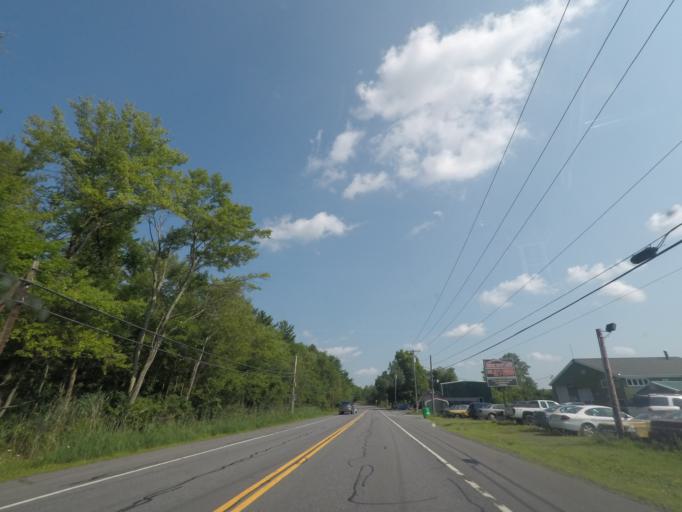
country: US
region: New York
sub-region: Rensselaer County
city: Nassau
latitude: 42.5314
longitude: -73.6571
